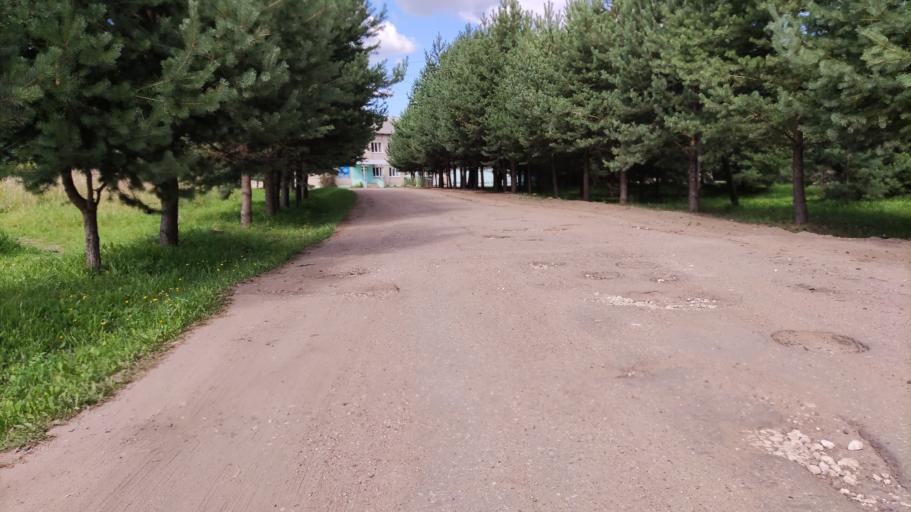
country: RU
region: Tverskaya
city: Rzhev
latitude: 56.2364
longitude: 34.3314
